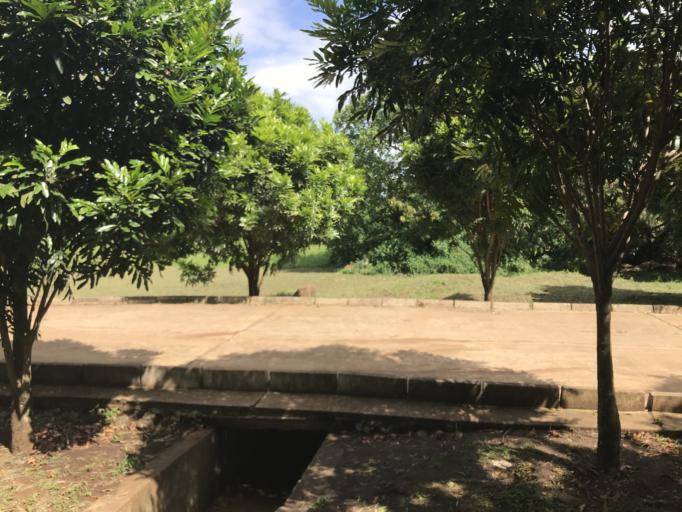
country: TZ
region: Arusha
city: Usa River
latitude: -3.4016
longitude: 36.7961
